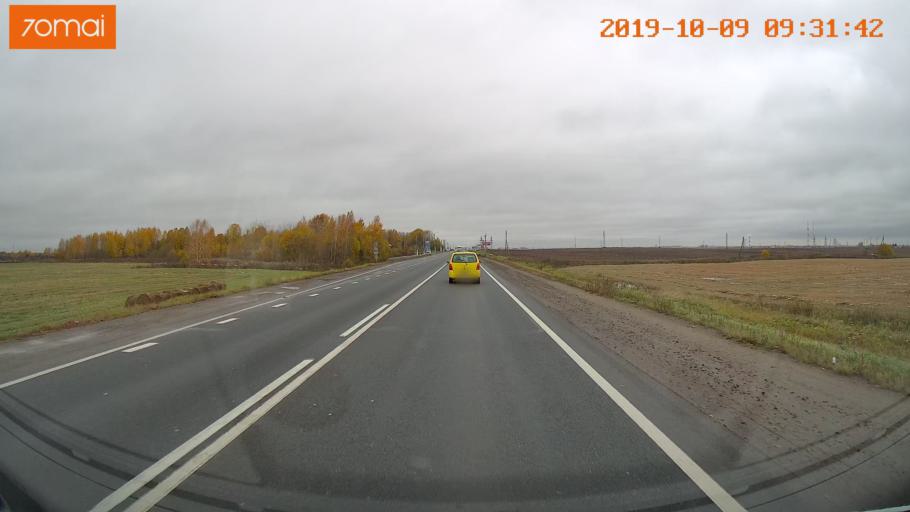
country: RU
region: Vologda
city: Vologda
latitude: 59.1518
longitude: 39.9361
